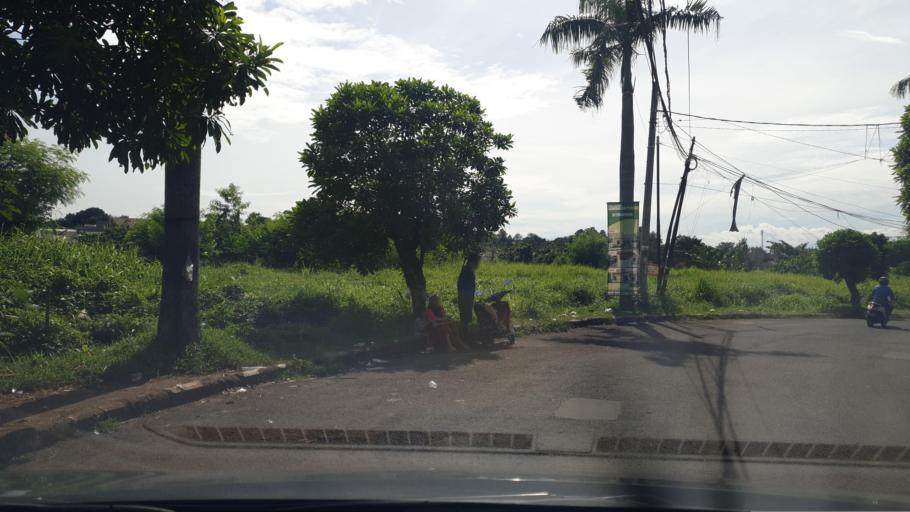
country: ID
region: West Java
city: Sawangan
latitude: -6.4035
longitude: 106.7724
